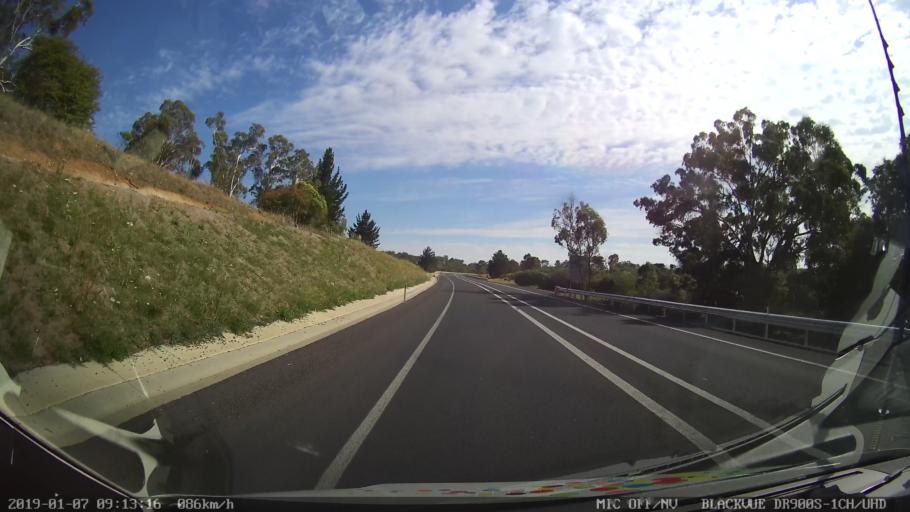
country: AU
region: New South Wales
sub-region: Armidale Dumaresq
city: Armidale
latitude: -30.6342
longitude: 151.5082
